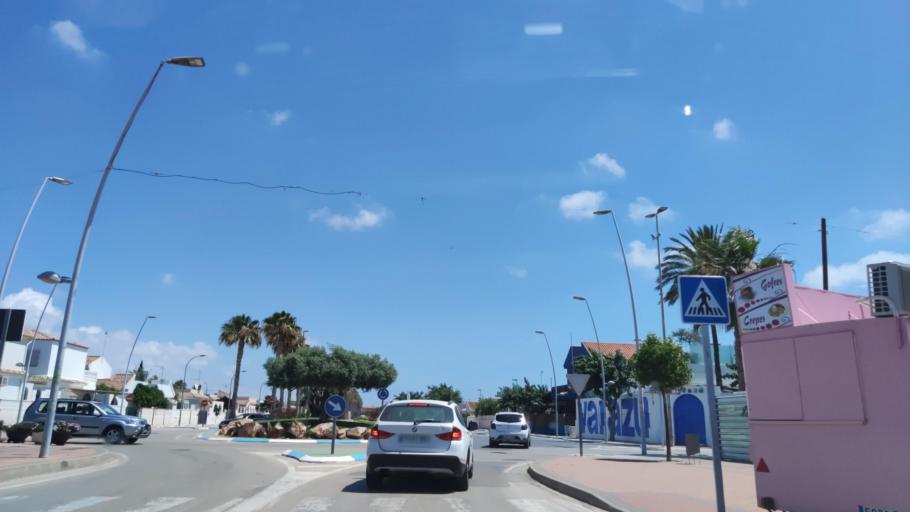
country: ES
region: Murcia
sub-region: Murcia
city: Los Alcazares
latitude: 37.7587
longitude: -0.8386
